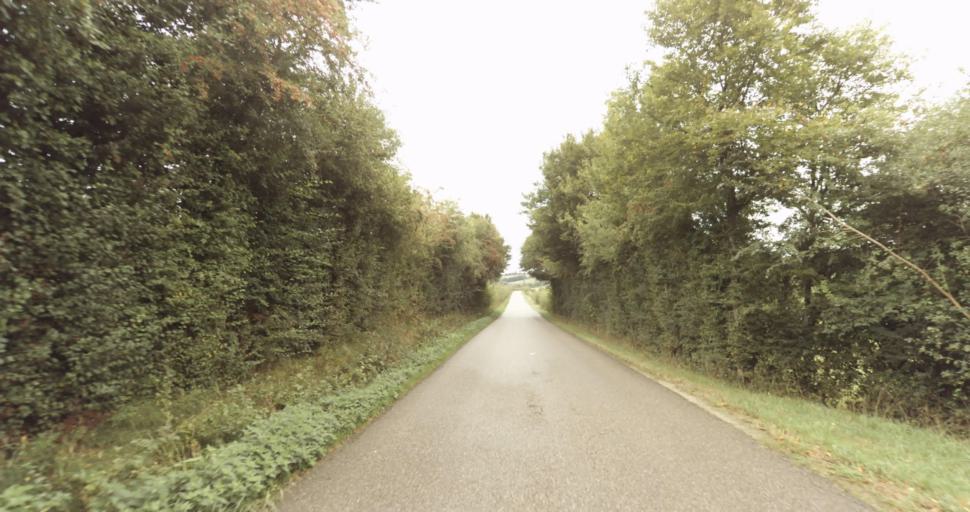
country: FR
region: Lower Normandy
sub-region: Departement de l'Orne
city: Vimoutiers
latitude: 48.8674
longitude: 0.2239
